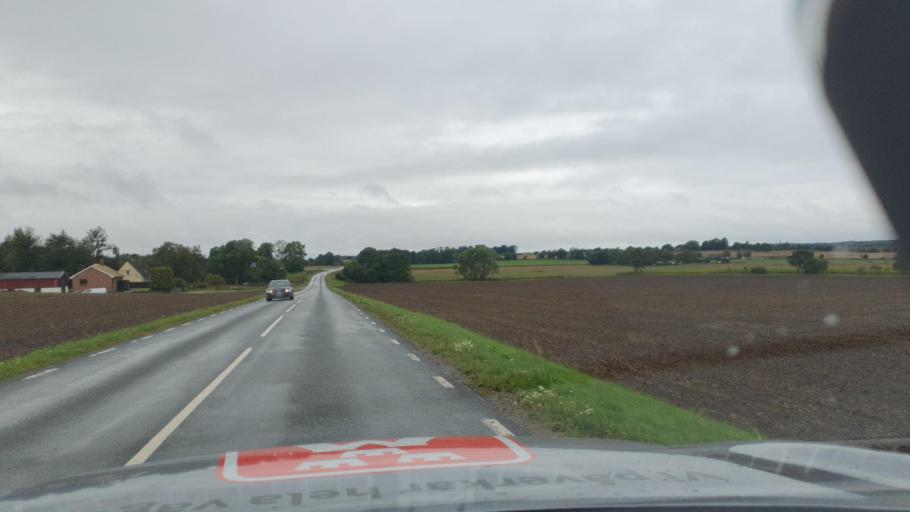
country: SE
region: Skane
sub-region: Simrishamns Kommun
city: Kivik
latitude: 55.5803
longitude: 14.1334
